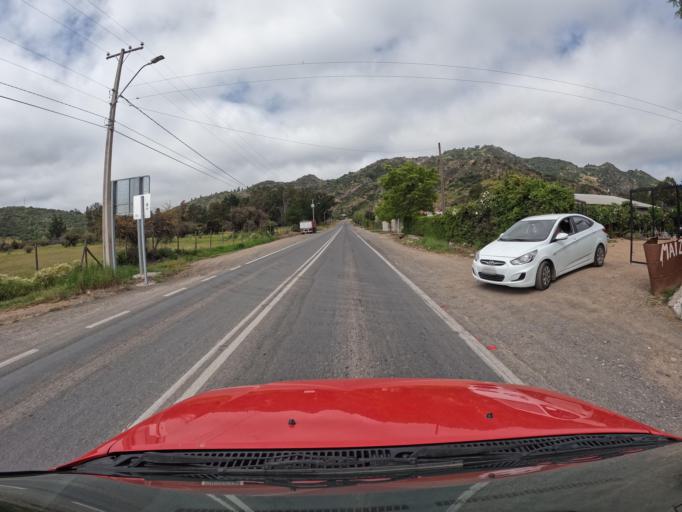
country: CL
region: O'Higgins
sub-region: Provincia de Colchagua
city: Santa Cruz
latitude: -34.6590
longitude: -71.4107
